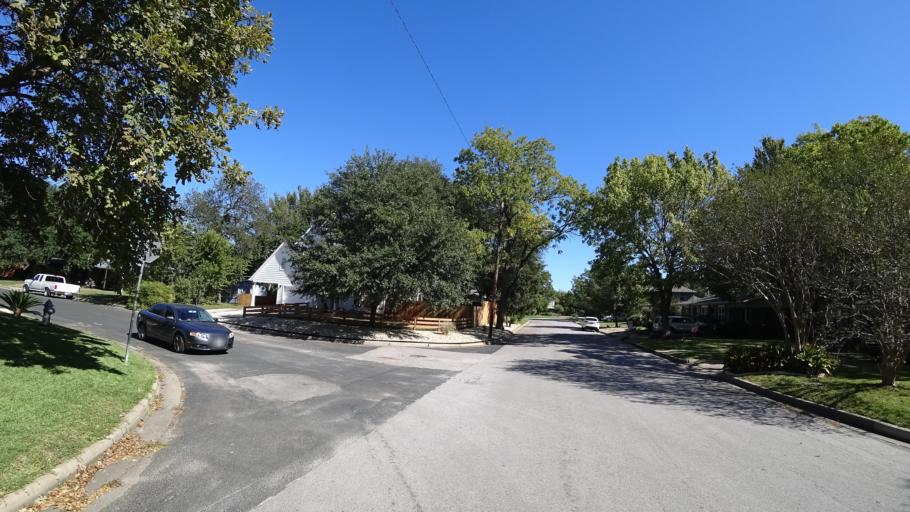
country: US
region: Texas
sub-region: Travis County
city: West Lake Hills
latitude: 30.3249
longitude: -97.7536
